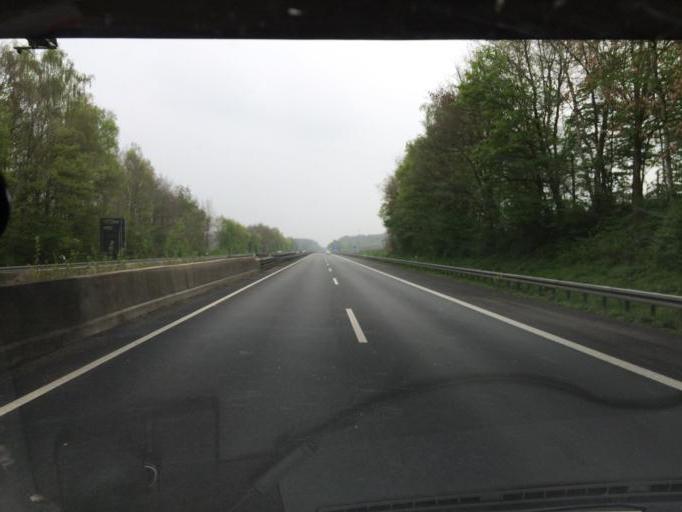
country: DE
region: North Rhine-Westphalia
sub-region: Regierungsbezirk Munster
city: Haltern
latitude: 51.7794
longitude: 7.1771
